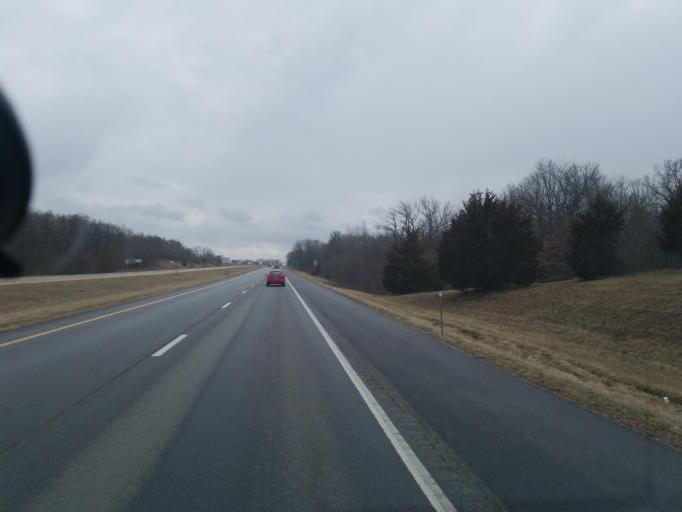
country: US
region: Missouri
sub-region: Randolph County
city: Moberly
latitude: 39.3880
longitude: -92.4134
